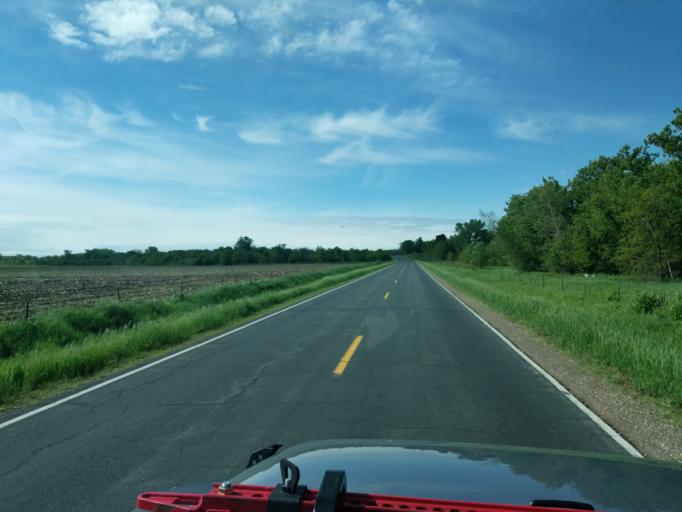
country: US
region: Wisconsin
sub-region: Saint Croix County
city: Hammond
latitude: 44.9029
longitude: -92.4862
